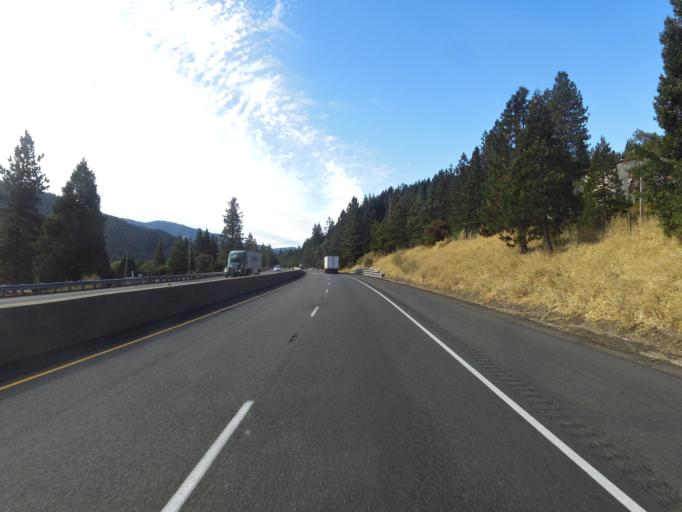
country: US
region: California
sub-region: Siskiyou County
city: Dunsmuir
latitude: 41.2110
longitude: -122.2751
